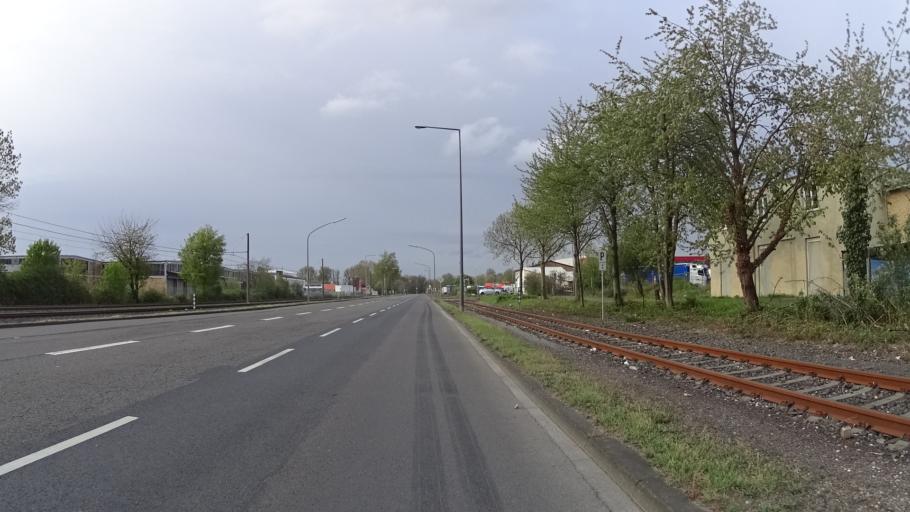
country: DE
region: North Rhine-Westphalia
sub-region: Regierungsbezirk Koln
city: Nippes
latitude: 51.0006
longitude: 6.9549
